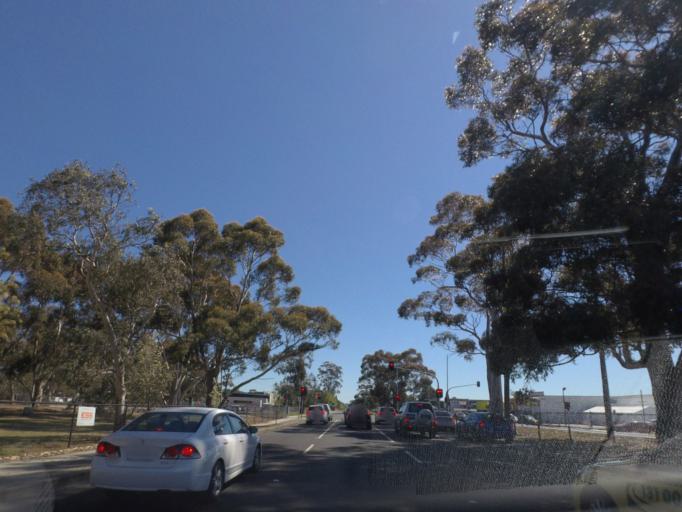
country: AU
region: Victoria
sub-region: Moreland
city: Fawkner
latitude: -37.7154
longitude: 144.9621
